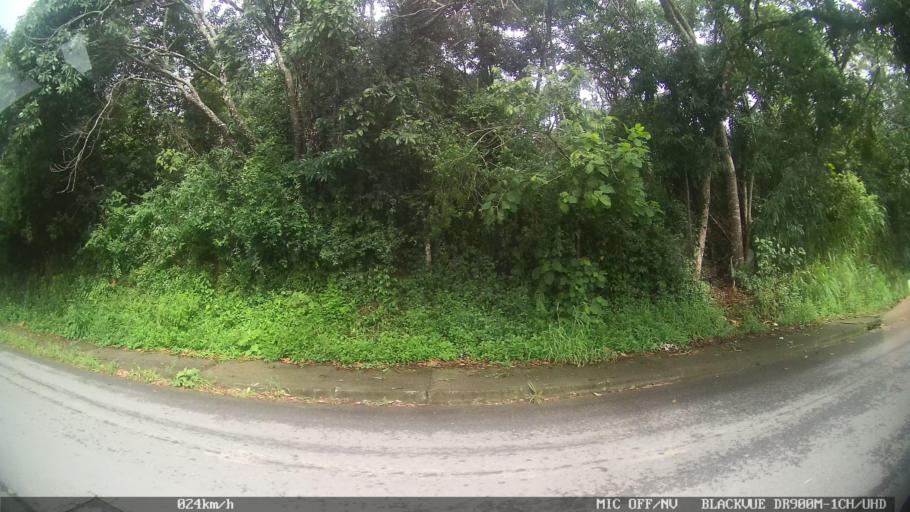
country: BR
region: Santa Catarina
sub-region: Biguacu
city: Biguacu
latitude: -27.5263
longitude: -48.6544
